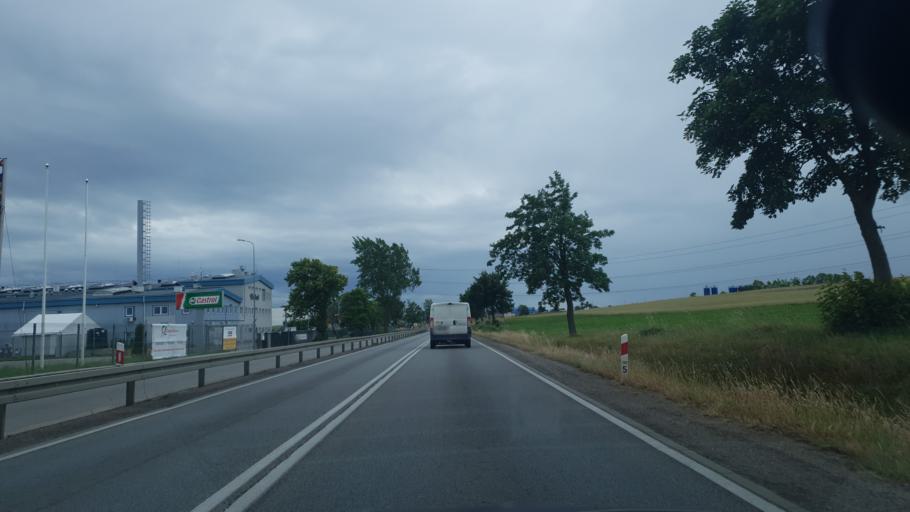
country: PL
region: Pomeranian Voivodeship
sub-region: Powiat kartuski
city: Zukowo
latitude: 54.3838
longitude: 18.3611
